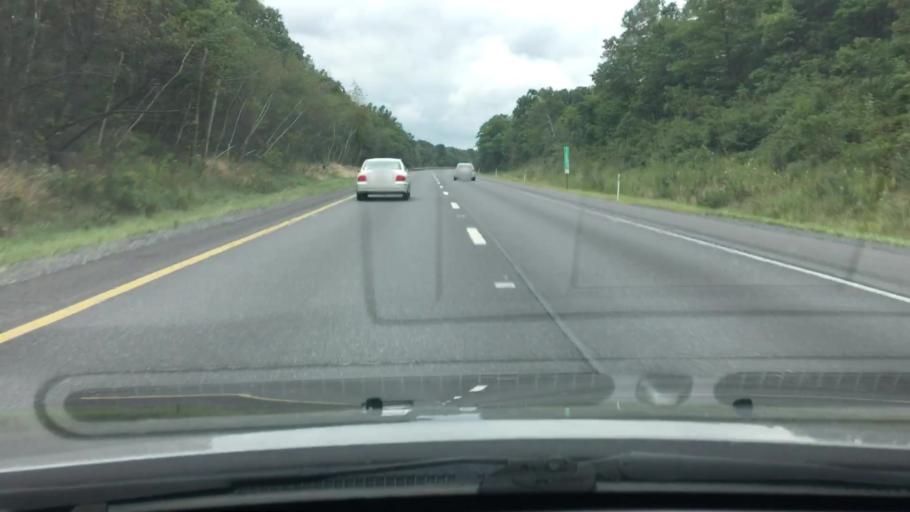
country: US
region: Pennsylvania
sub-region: Schuylkill County
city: Mahanoy City
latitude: 40.7898
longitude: -76.1421
